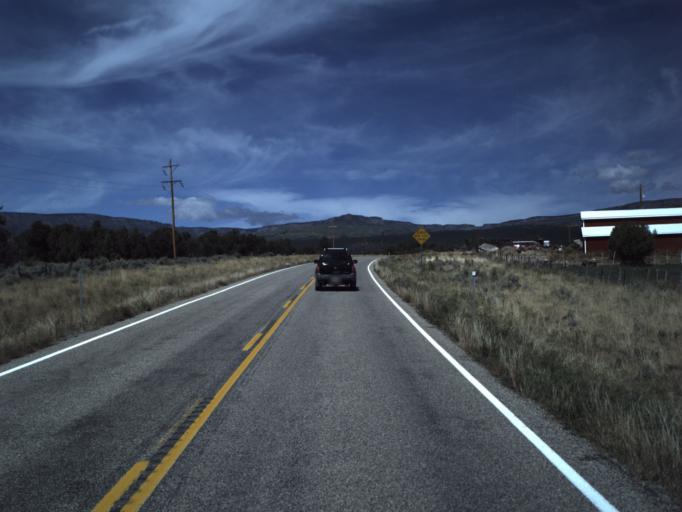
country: US
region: Utah
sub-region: Wayne County
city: Loa
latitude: 37.9528
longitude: -111.4348
